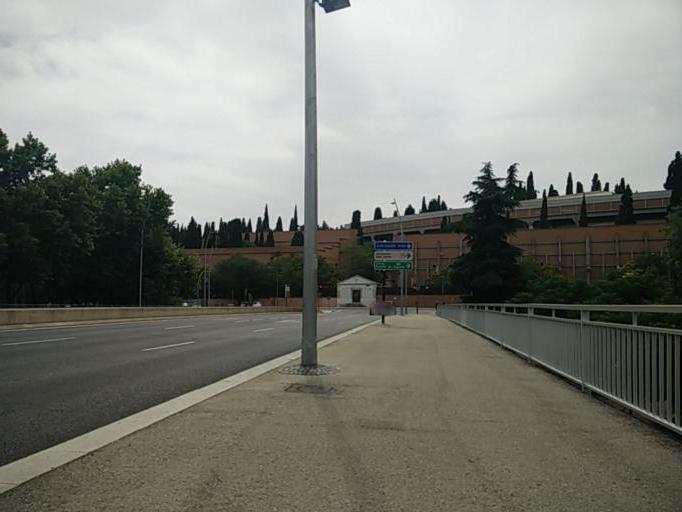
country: ES
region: Madrid
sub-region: Provincia de Madrid
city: Carabanchel
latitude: 40.4038
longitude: -3.7236
